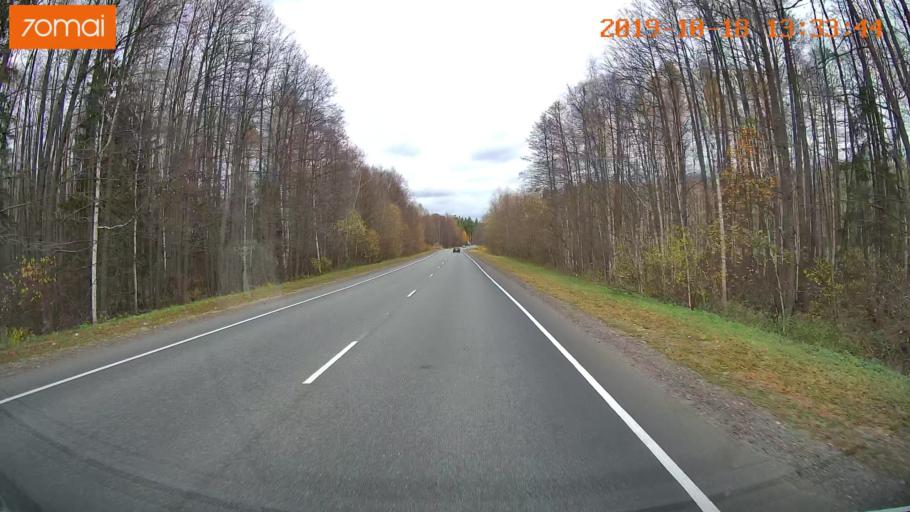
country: RU
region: Rjazan
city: Solotcha
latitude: 54.8469
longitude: 39.9416
